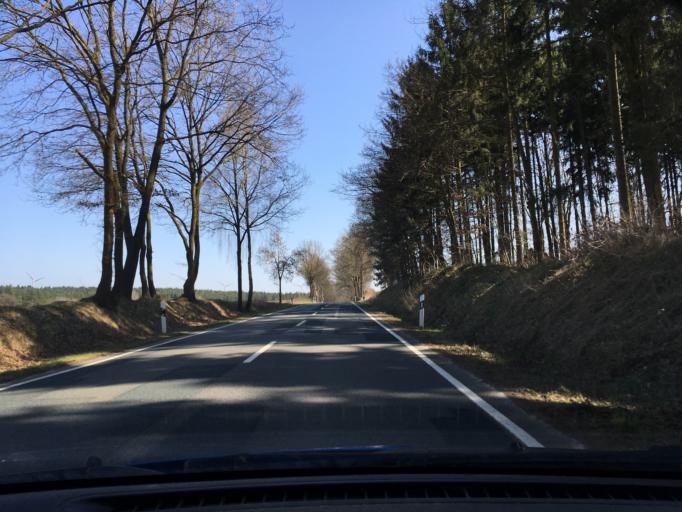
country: DE
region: Lower Saxony
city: Rehlingen
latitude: 53.1127
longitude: 10.2394
